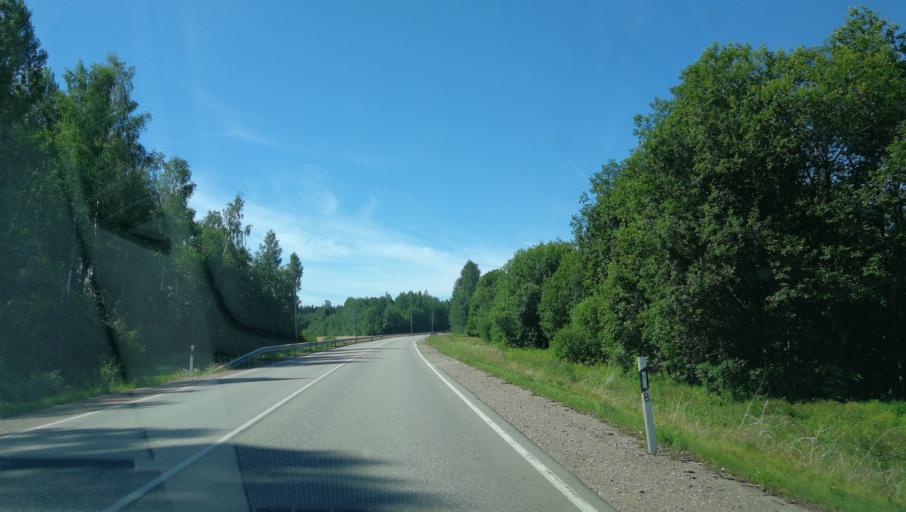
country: LV
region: Gulbenes Rajons
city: Gulbene
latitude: 57.1461
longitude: 26.7197
